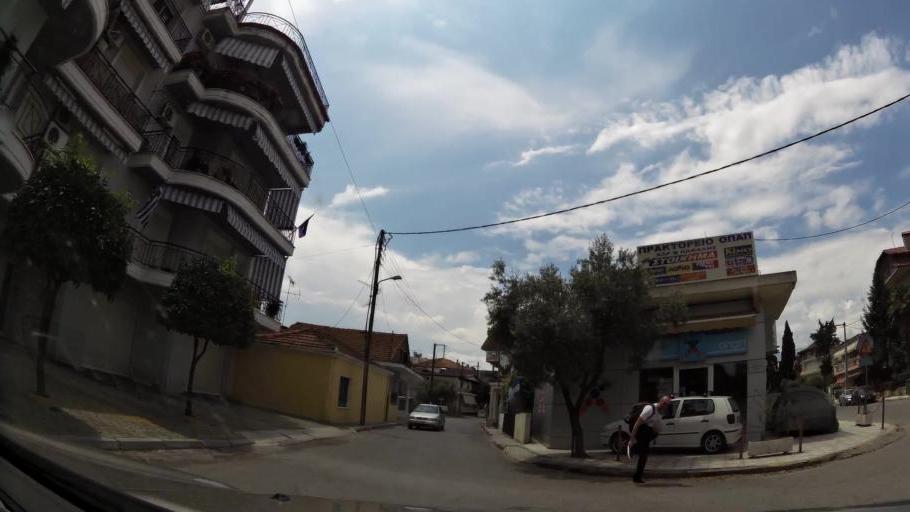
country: GR
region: Central Macedonia
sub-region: Nomos Pierias
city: Katerini
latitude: 40.2660
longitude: 22.5150
